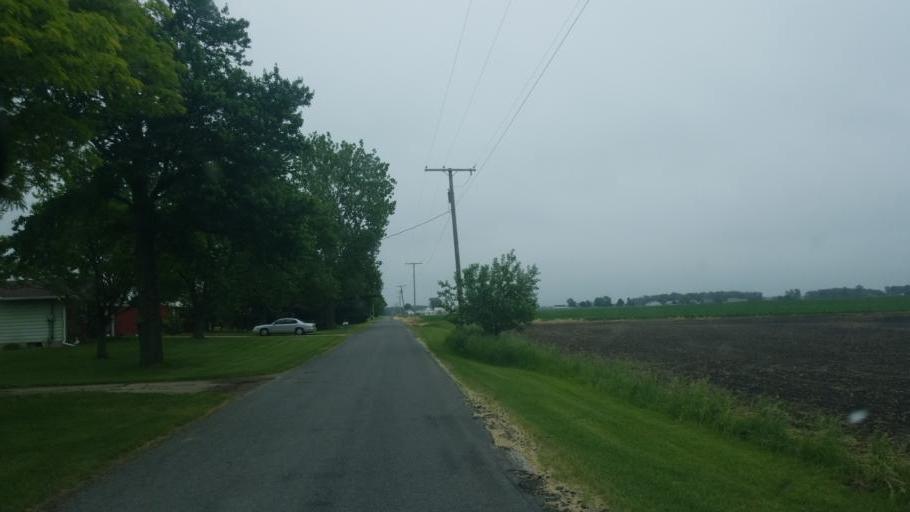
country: US
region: Indiana
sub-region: Marshall County
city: Bremen
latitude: 41.5079
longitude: -86.1333
